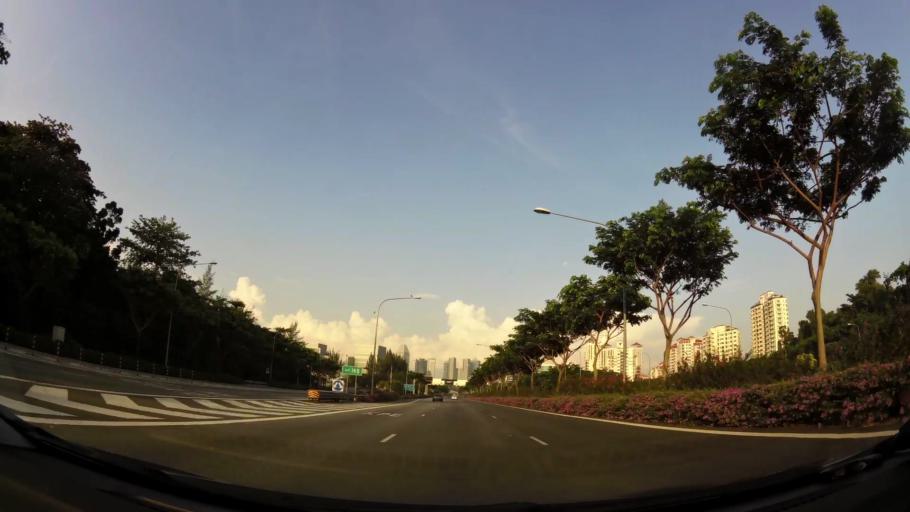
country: SG
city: Singapore
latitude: 1.2954
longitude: 103.8785
